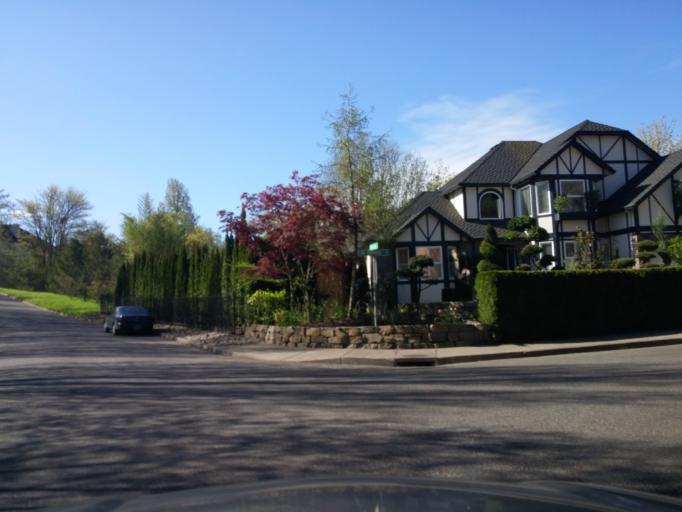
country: US
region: Oregon
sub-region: Washington County
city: West Haven
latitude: 45.5364
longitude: -122.7842
